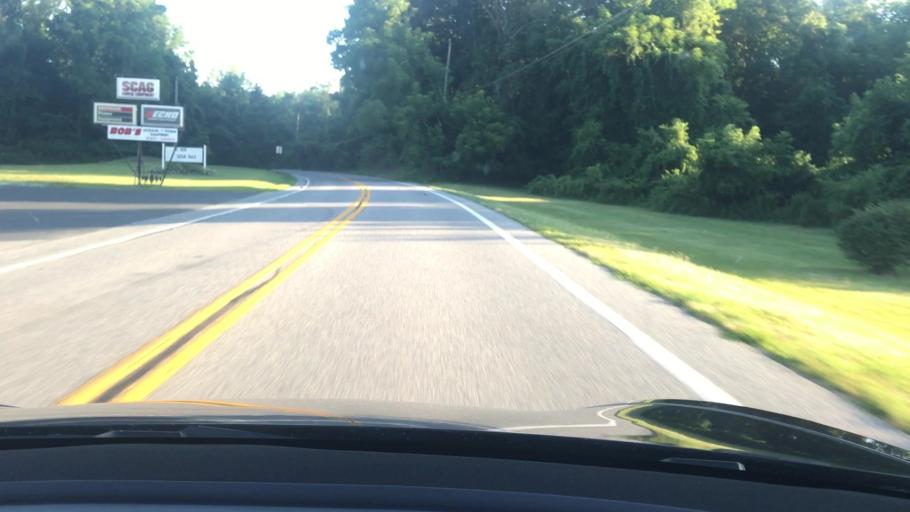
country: US
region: Pennsylvania
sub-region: York County
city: Dover
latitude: 40.0829
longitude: -76.8745
